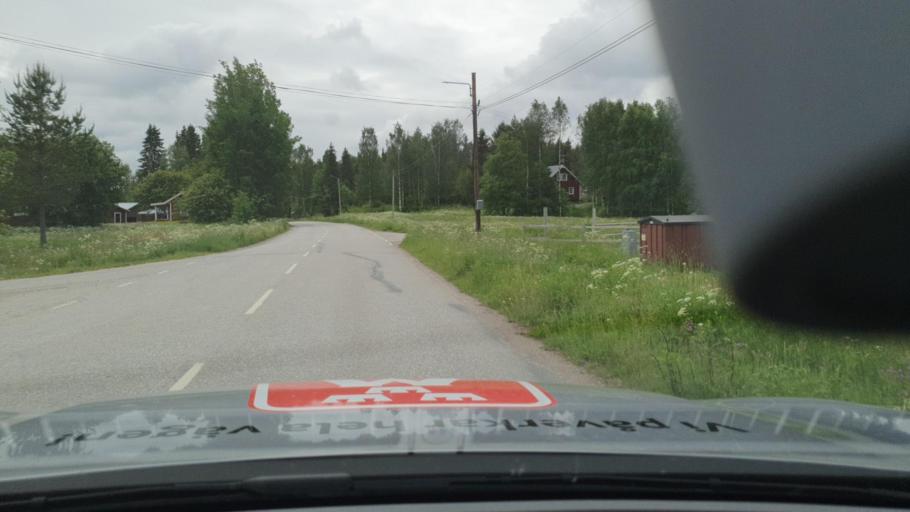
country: SE
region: Norrbotten
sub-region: Lulea Kommun
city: Ranea
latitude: 65.9020
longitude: 22.1804
